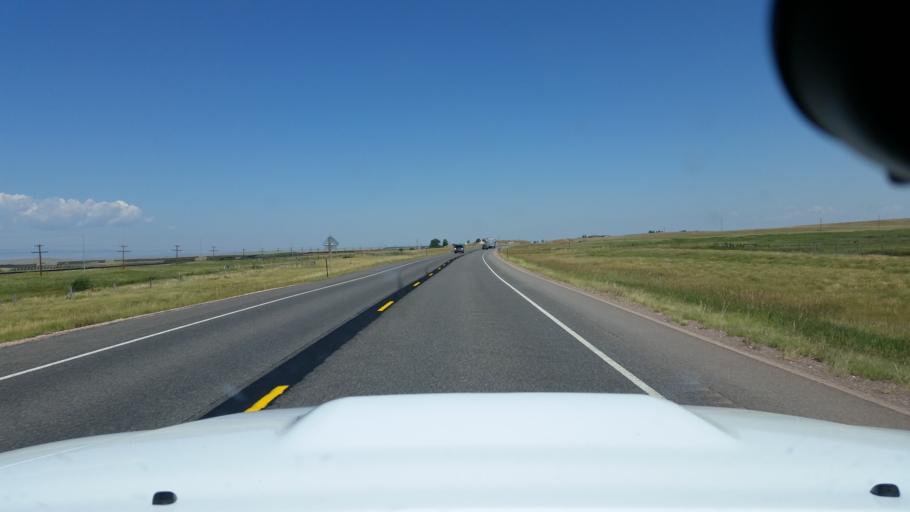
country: US
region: Wyoming
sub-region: Albany County
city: Laramie
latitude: 41.1730
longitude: -105.5879
